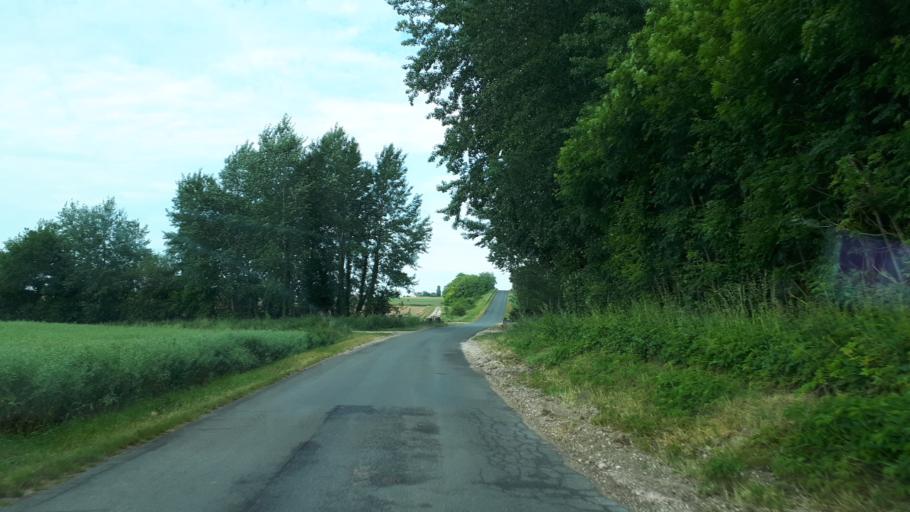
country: FR
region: Centre
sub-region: Departement du Loir-et-Cher
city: Villiers-sur-Loir
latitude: 47.7550
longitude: 0.9995
